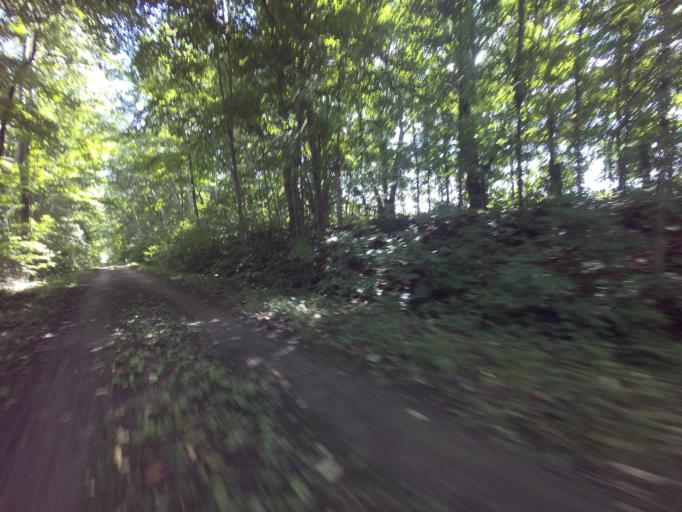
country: CA
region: Ontario
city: Orangeville
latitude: 43.7898
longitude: -80.2585
